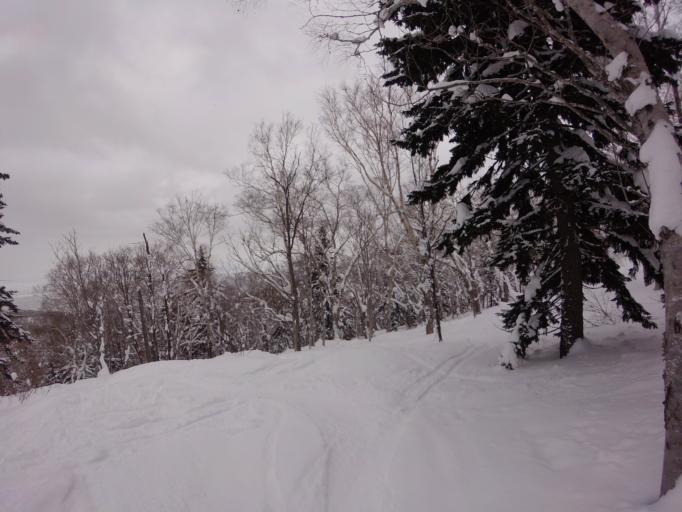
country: JP
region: Hokkaido
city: Sapporo
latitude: 43.0706
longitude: 141.2050
